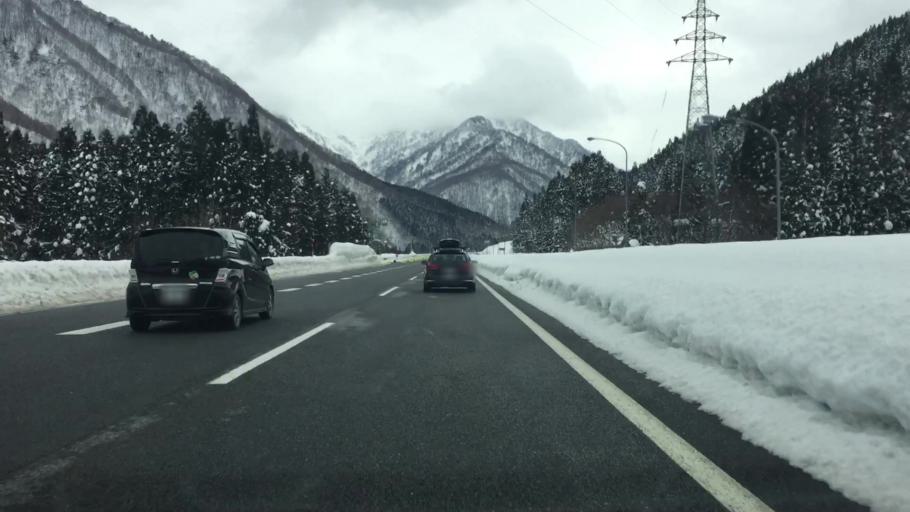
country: JP
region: Niigata
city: Shiozawa
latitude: 36.8802
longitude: 138.8555
